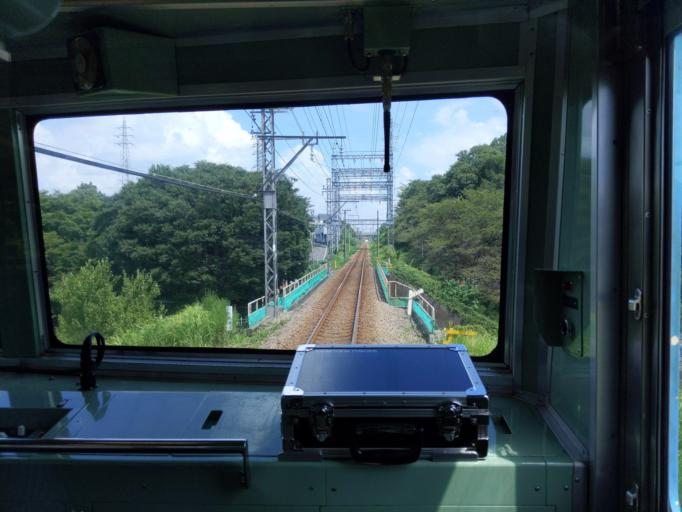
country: JP
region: Tokyo
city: Kamirenjaku
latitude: 35.6882
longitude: 139.5226
